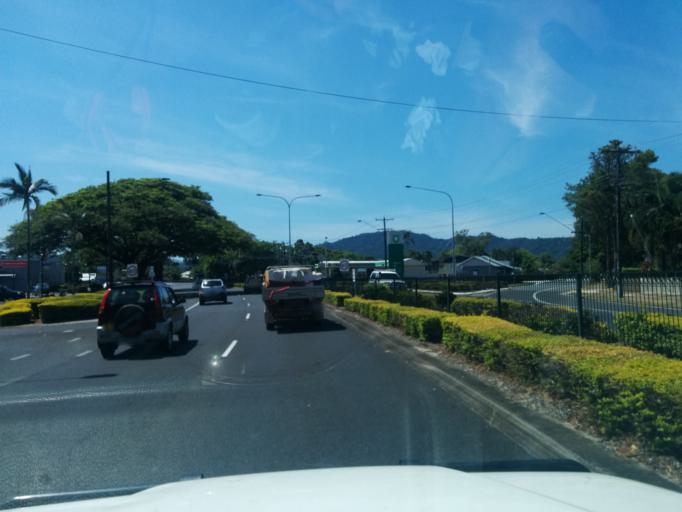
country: AU
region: Queensland
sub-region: Cairns
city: Cairns
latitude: -16.9266
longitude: 145.7419
